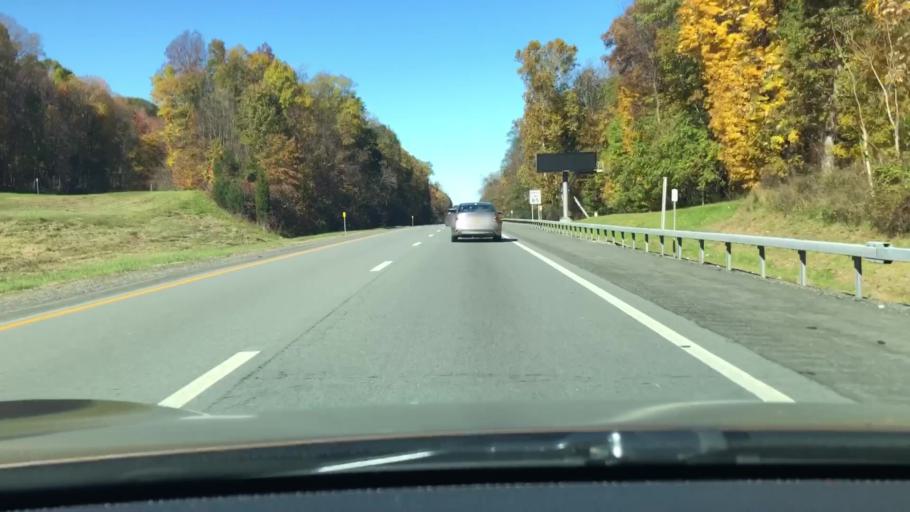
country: US
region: New York
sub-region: Orange County
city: Vails Gate
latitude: 41.4711
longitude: -74.0730
